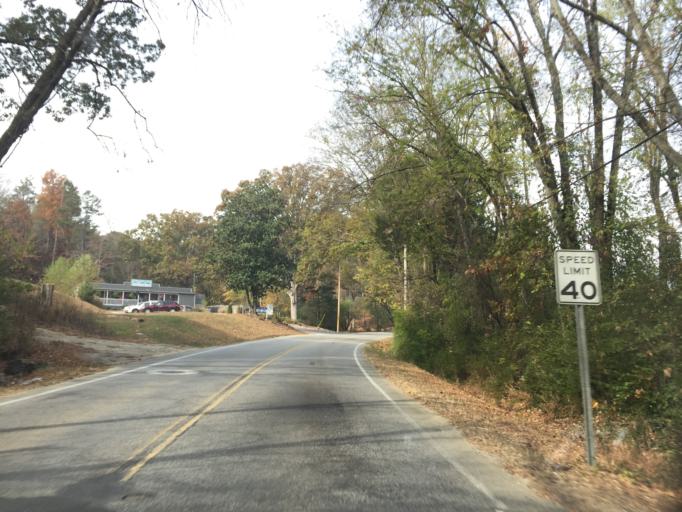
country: US
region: Tennessee
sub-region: Hamilton County
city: Collegedale
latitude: 35.0843
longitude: -85.0772
